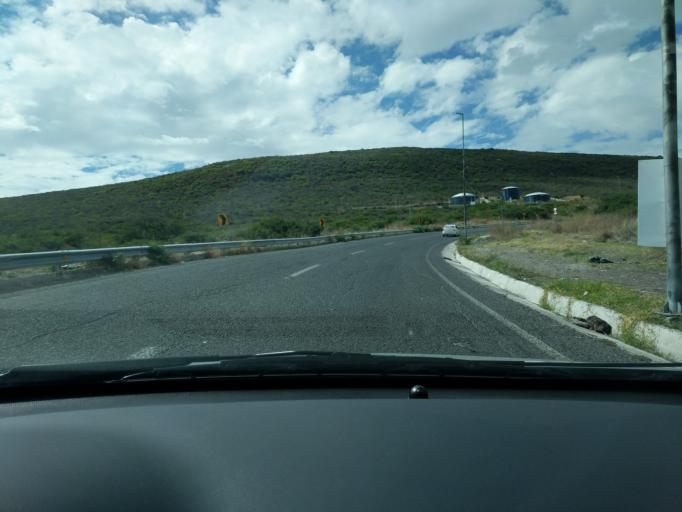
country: MX
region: Queretaro
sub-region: El Marques
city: La Pradera
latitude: 20.6603
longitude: -100.3434
